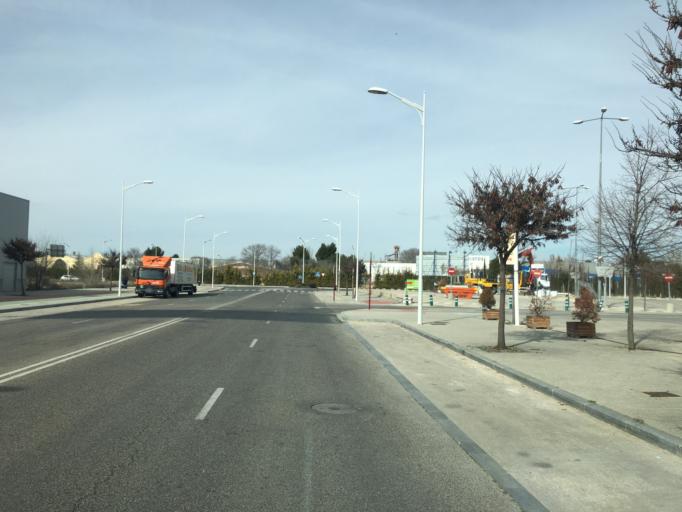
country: ES
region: Castille-La Mancha
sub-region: Provincia de Albacete
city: Albacete
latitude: 39.0082
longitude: -1.8813
